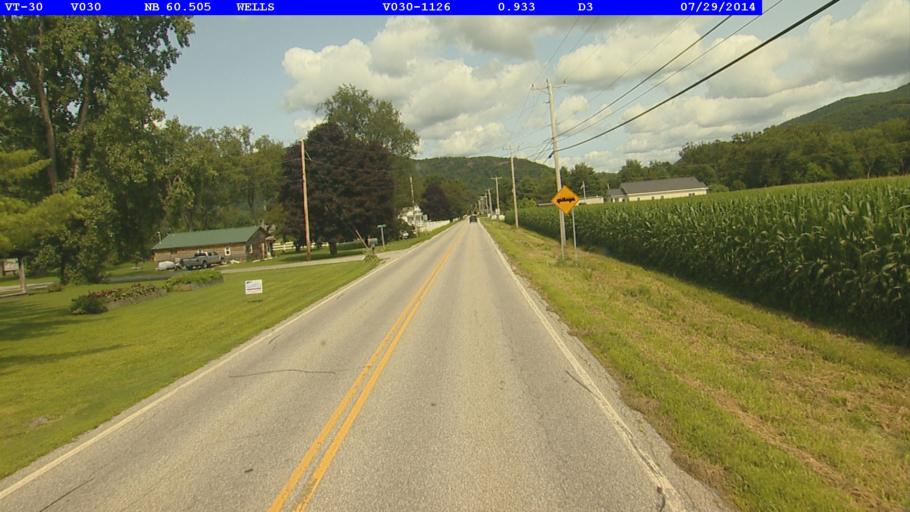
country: US
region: New York
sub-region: Washington County
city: Granville
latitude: 43.4167
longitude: -73.2146
